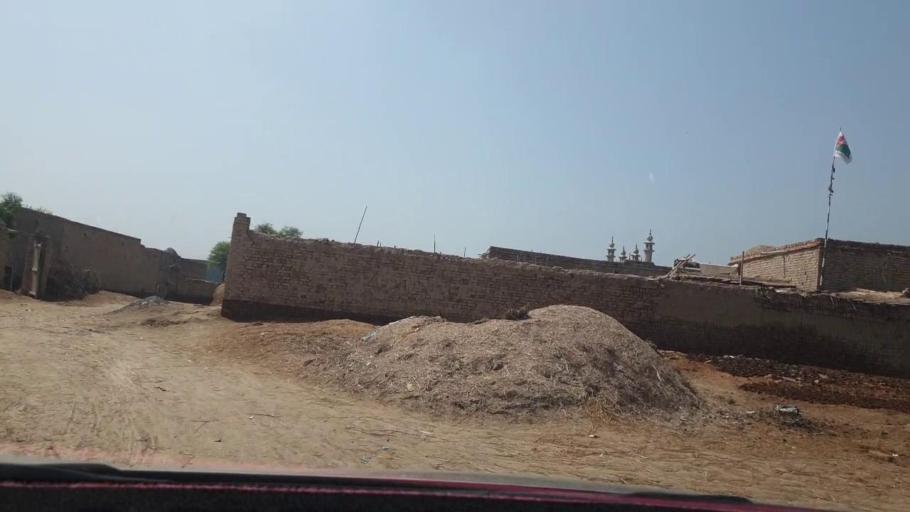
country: PK
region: Sindh
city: Warah
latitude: 27.3953
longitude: 67.8462
